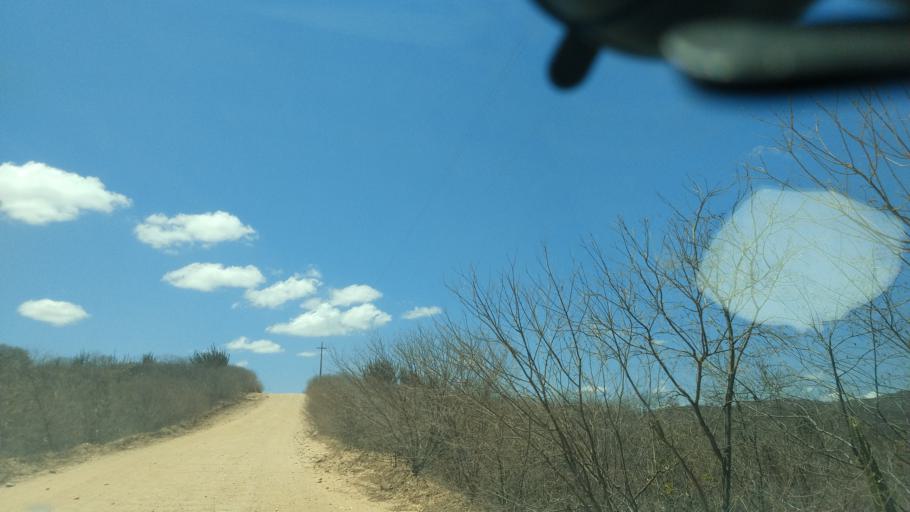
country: BR
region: Rio Grande do Norte
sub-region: Cerro Cora
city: Cerro Cora
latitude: -6.0100
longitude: -36.2921
